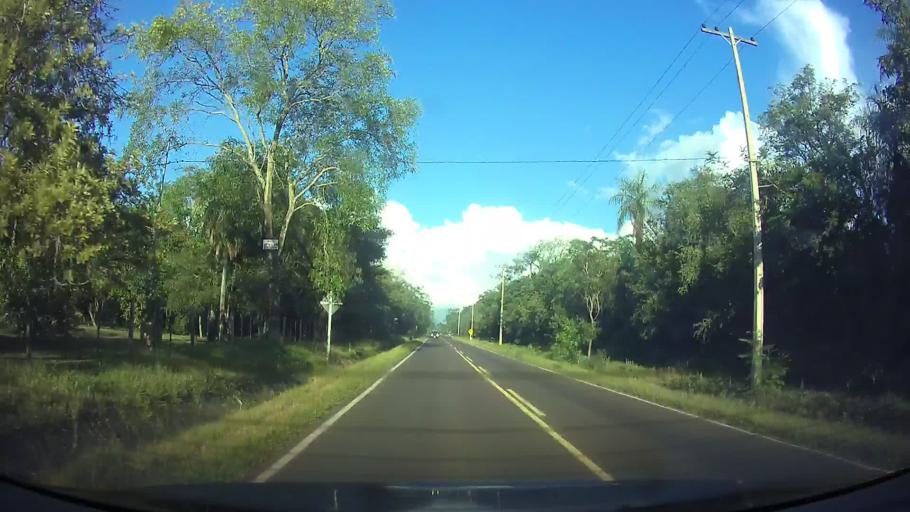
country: PY
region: Cordillera
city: Emboscada
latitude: -25.2042
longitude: -57.3424
